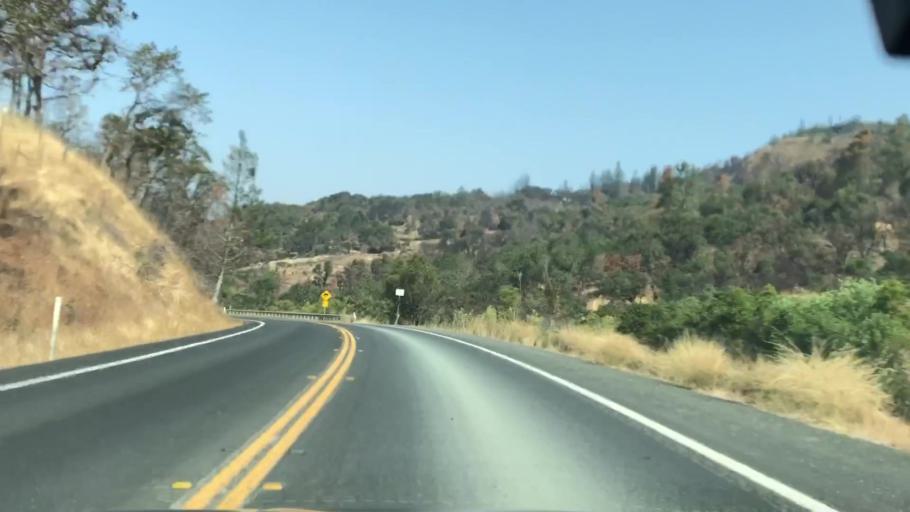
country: US
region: California
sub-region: Sonoma County
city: Larkfield-Wikiup
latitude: 38.5553
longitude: -122.6758
